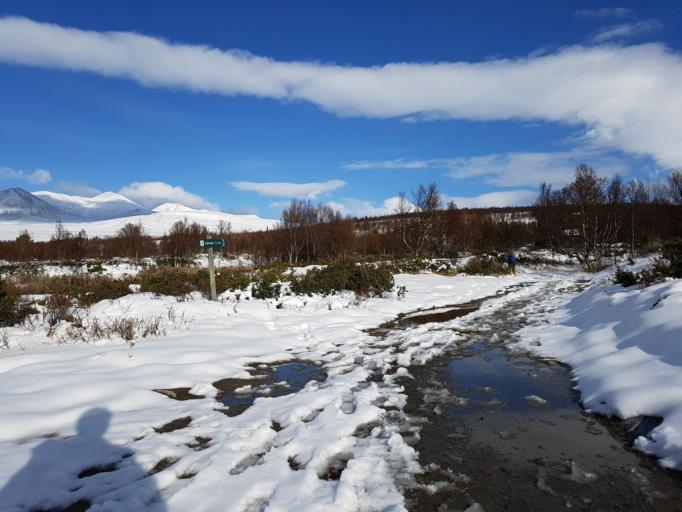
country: NO
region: Oppland
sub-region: Sel
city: Otta
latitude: 61.8255
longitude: 9.6805
